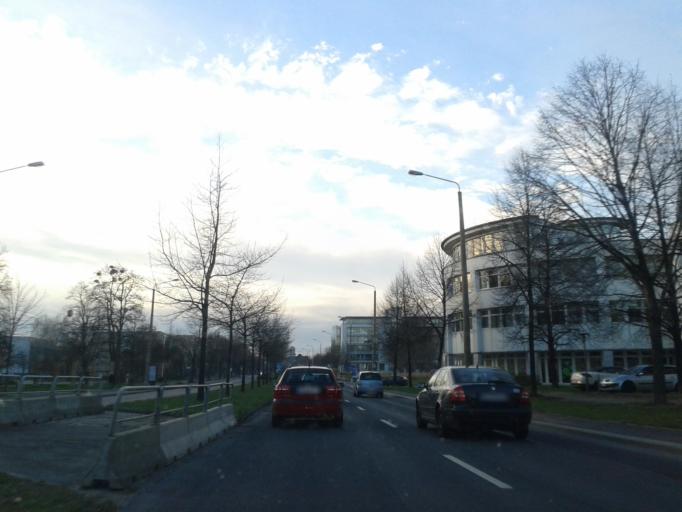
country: DE
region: Saxony
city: Dresden
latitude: 51.0288
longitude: 13.7432
